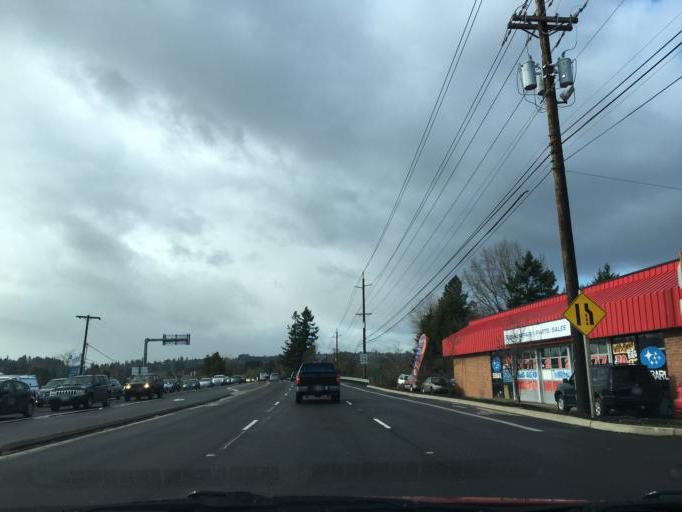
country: US
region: Oregon
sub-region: Washington County
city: Tigard
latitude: 45.4330
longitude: -122.7679
